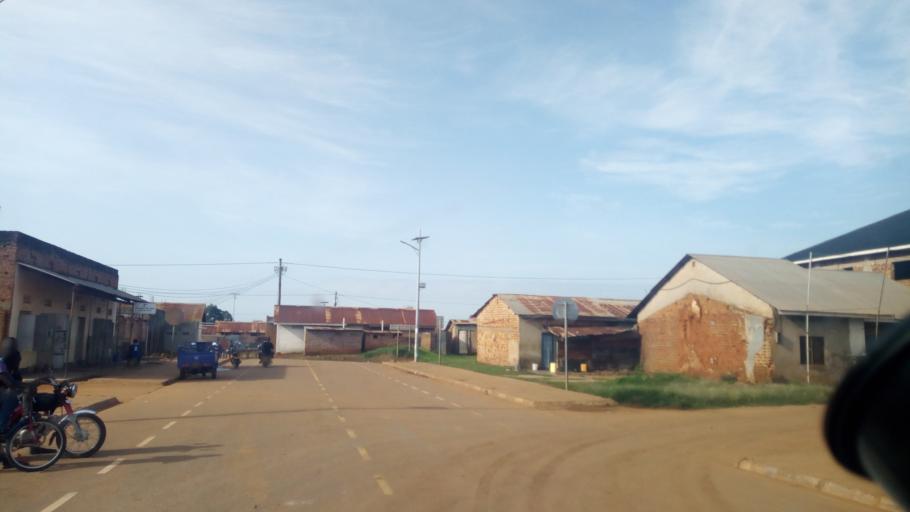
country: UG
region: Northern Region
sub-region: Gulu District
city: Gulu
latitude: 2.7677
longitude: 32.3021
